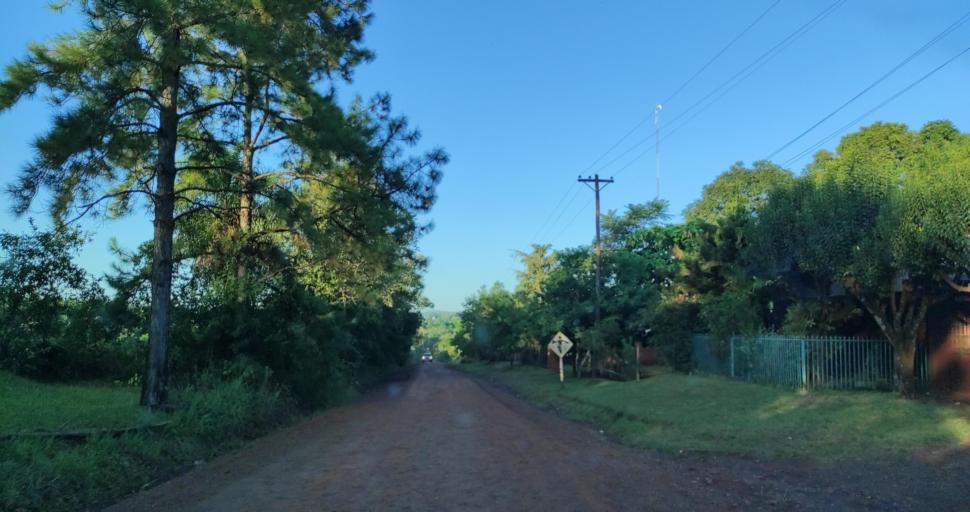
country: AR
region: Misiones
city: Gobernador Roca
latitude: -27.2243
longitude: -55.4312
